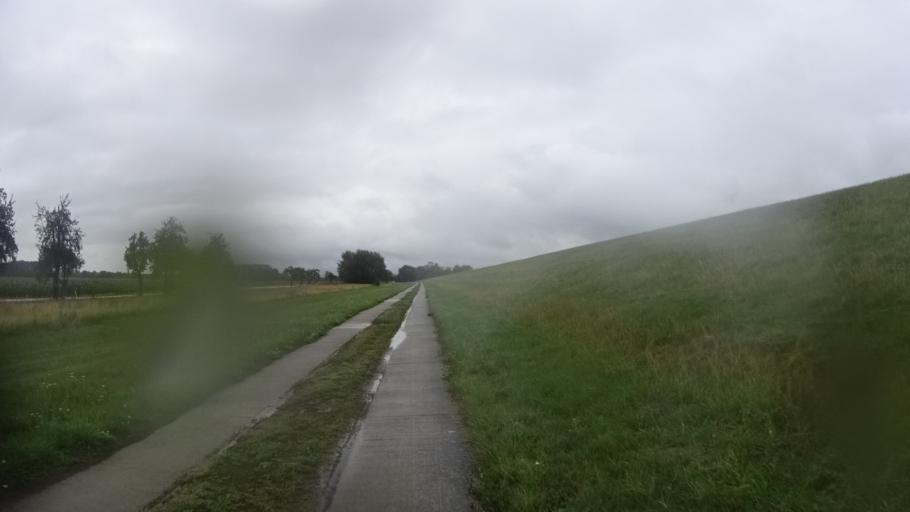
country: DE
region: Lower Saxony
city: Damnatz
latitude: 53.1754
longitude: 11.1338
